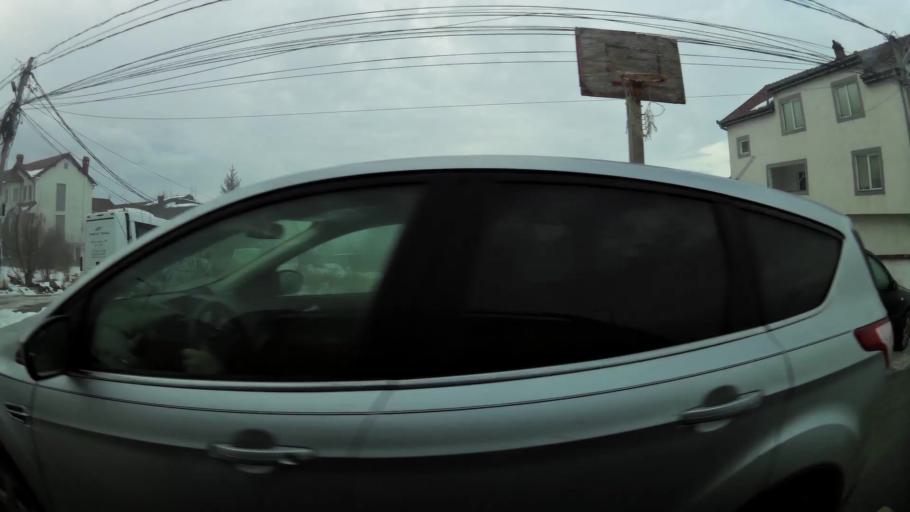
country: XK
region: Pristina
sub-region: Komuna e Prishtines
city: Pristina
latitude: 42.6622
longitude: 21.1457
